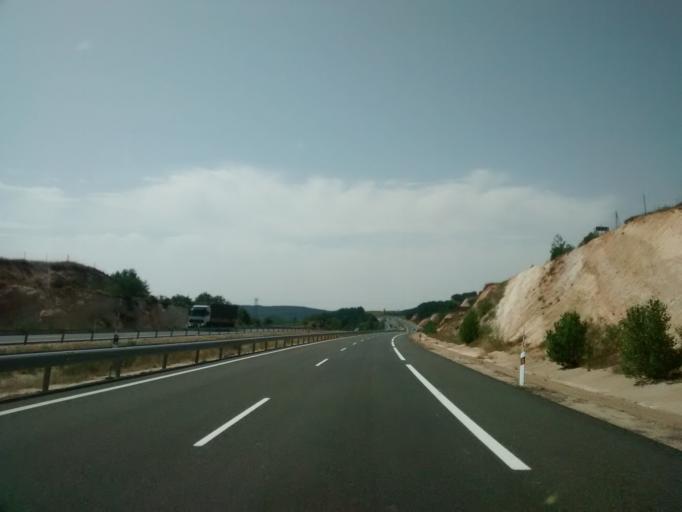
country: ES
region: Castille and Leon
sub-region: Provincia de Palencia
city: Aguilar de Campoo
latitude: 42.7410
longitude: -4.2899
